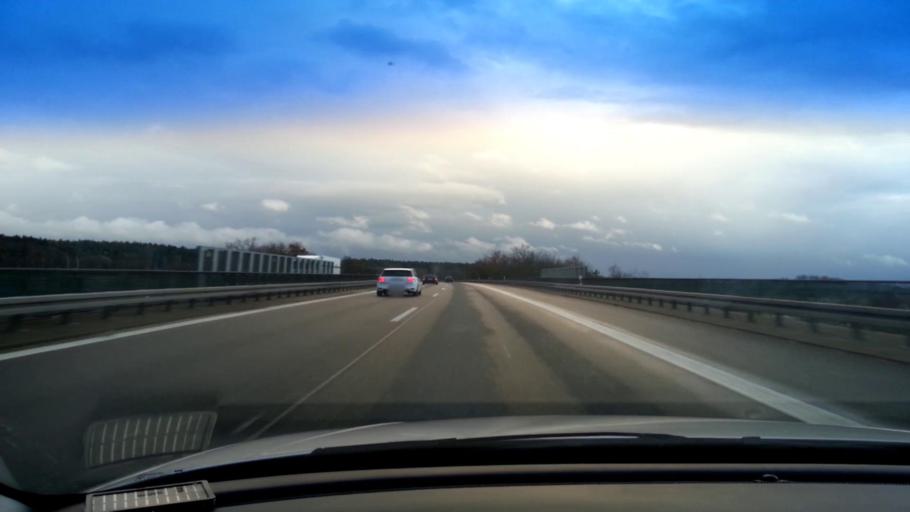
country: DE
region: Bavaria
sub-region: Upper Franconia
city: Kemmern
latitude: 49.9581
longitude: 10.8856
